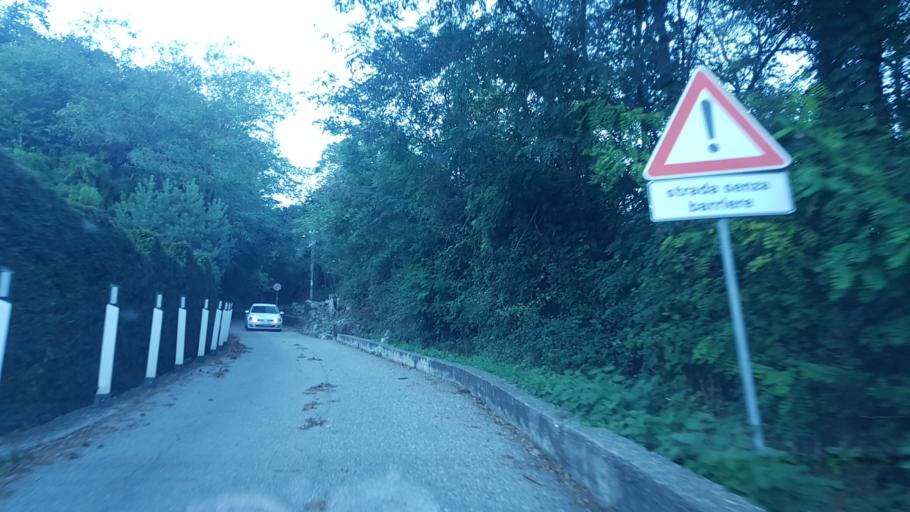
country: IT
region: Piedmont
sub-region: Provincia Verbano-Cusio-Ossola
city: Mergozzo
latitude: 45.9459
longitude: 8.4705
